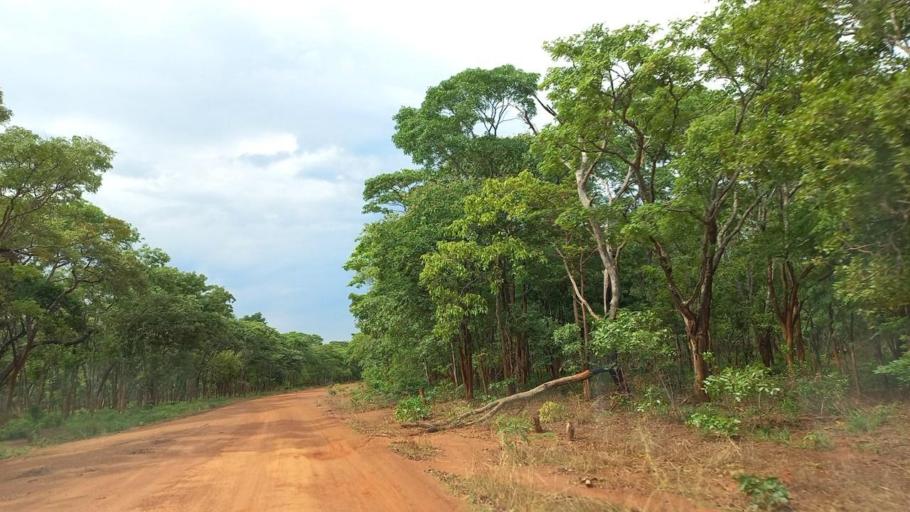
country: ZM
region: North-Western
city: Kalengwa
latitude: -13.4121
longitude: 25.0618
